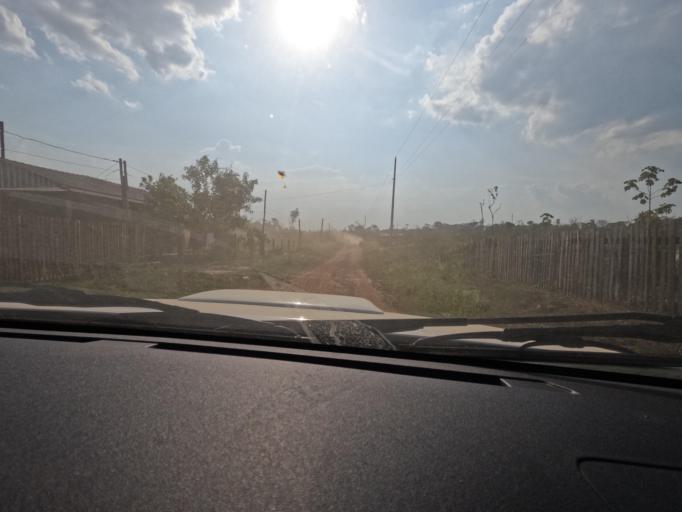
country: BR
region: Rondonia
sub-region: Porto Velho
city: Porto Velho
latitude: -8.5750
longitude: -63.9967
